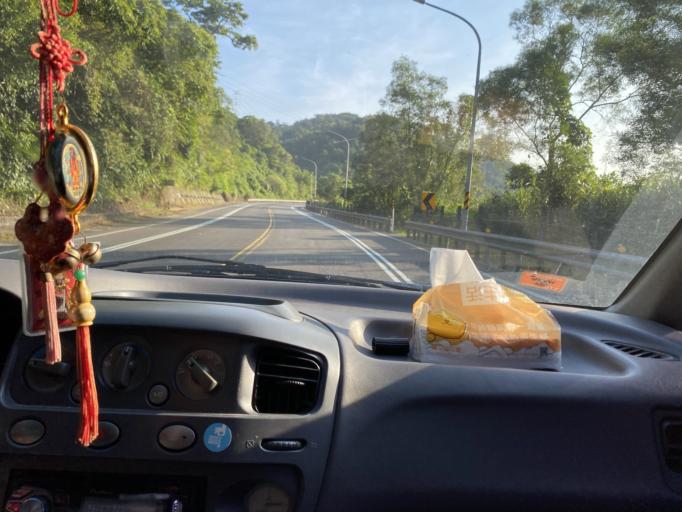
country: TW
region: Taiwan
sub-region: Keelung
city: Keelung
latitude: 25.0215
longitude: 121.8147
